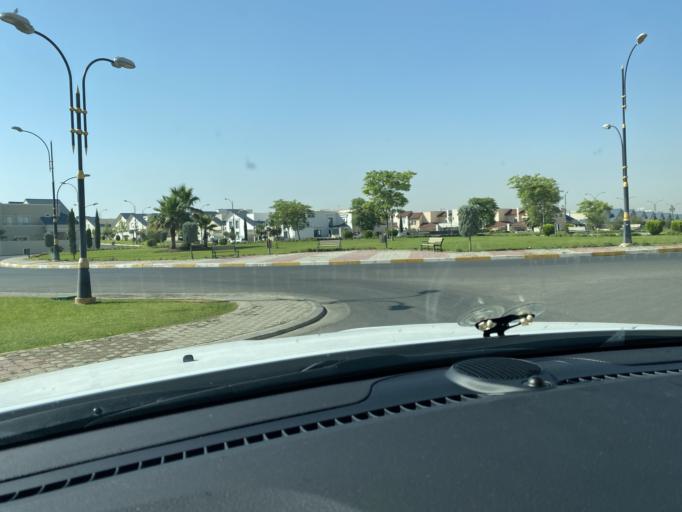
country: IQ
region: Arbil
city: Erbil
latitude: 36.2423
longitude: 44.0512
